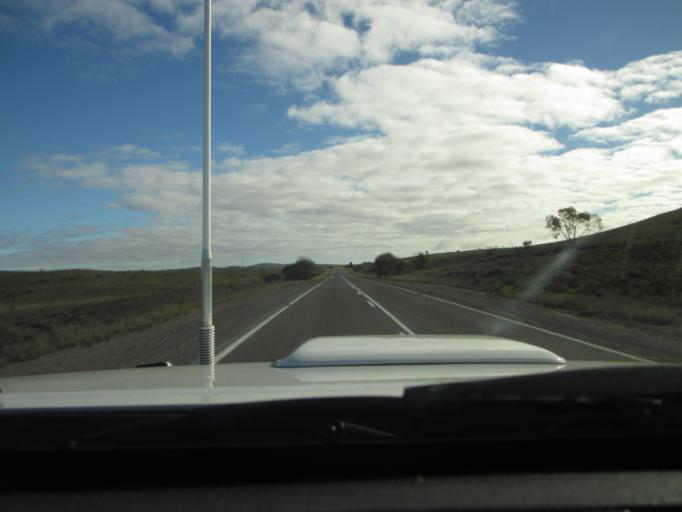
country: AU
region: South Australia
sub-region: Peterborough
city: Peterborough
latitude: -32.6103
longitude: 138.5707
